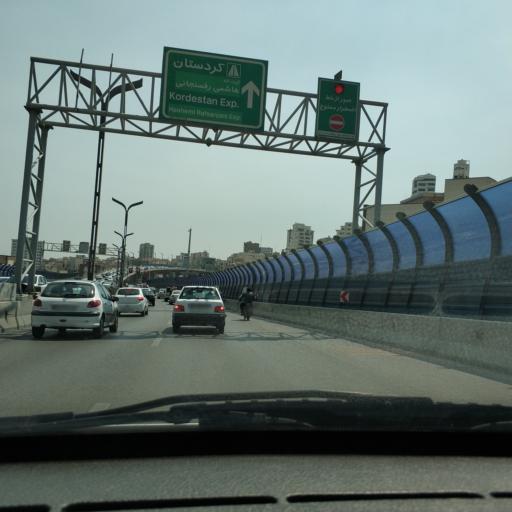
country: IR
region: Tehran
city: Tajrish
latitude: 35.7832
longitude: 51.4350
